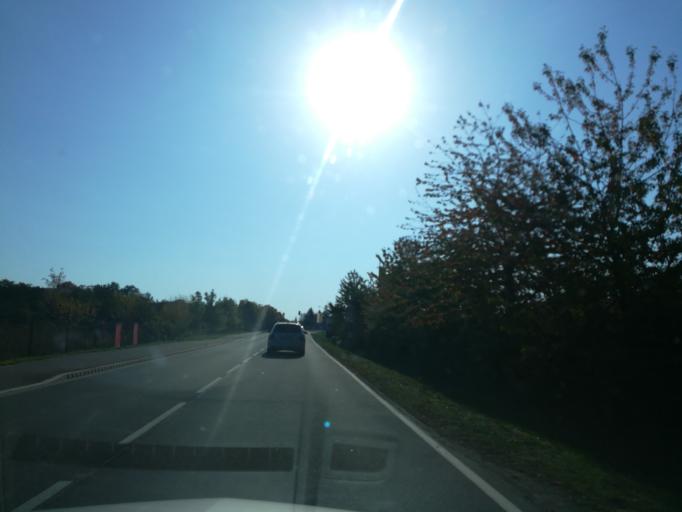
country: DE
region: Saxony-Anhalt
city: Gommern
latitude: 52.0838
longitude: 11.8132
